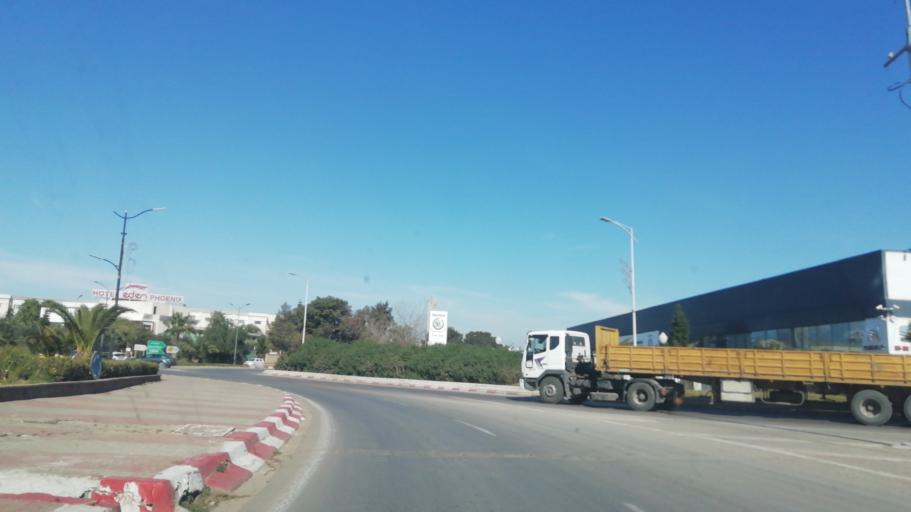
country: DZ
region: Oran
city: Es Senia
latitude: 35.6230
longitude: -0.5918
